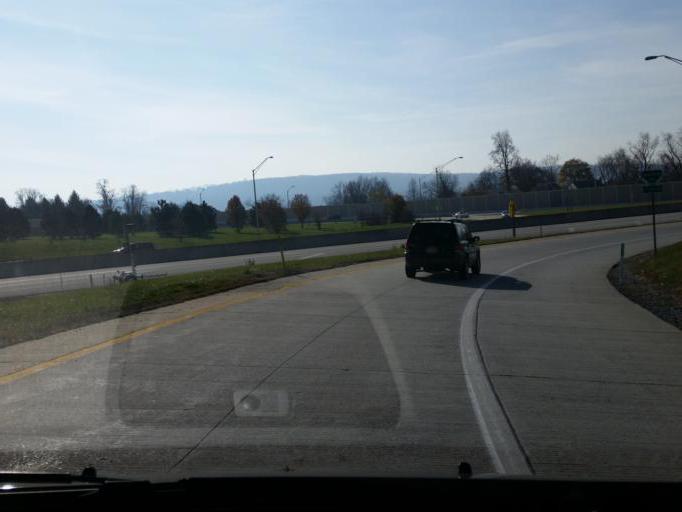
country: US
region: Pennsylvania
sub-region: Dauphin County
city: Highspire
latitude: 40.2156
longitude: -76.7869
